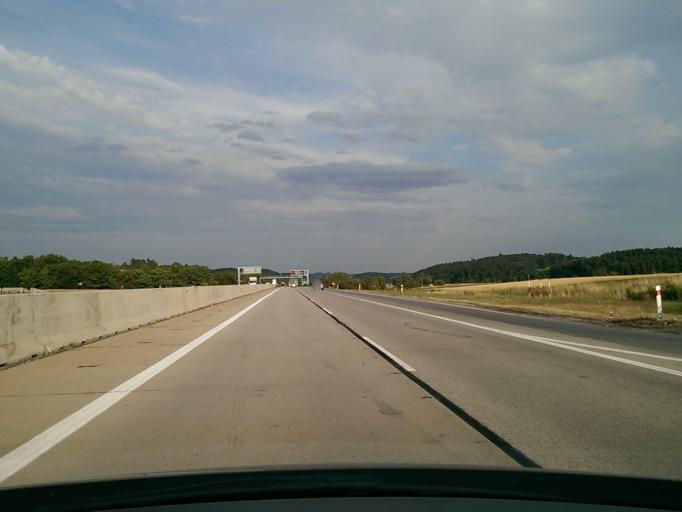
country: CZ
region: Vysocina
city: Merin
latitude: 49.3780
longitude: 15.9480
